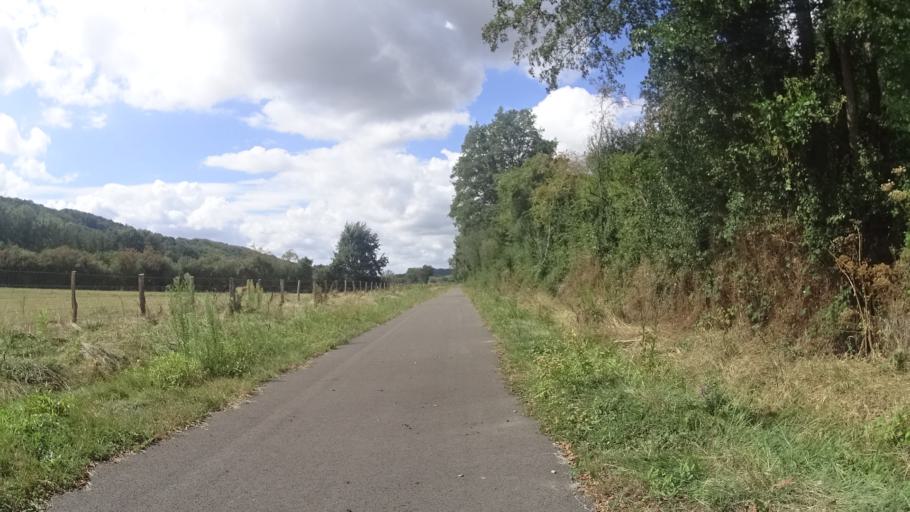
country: FR
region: Bourgogne
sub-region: Departement de Saone-et-Loire
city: Ecuisses
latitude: 46.8058
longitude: 4.5735
